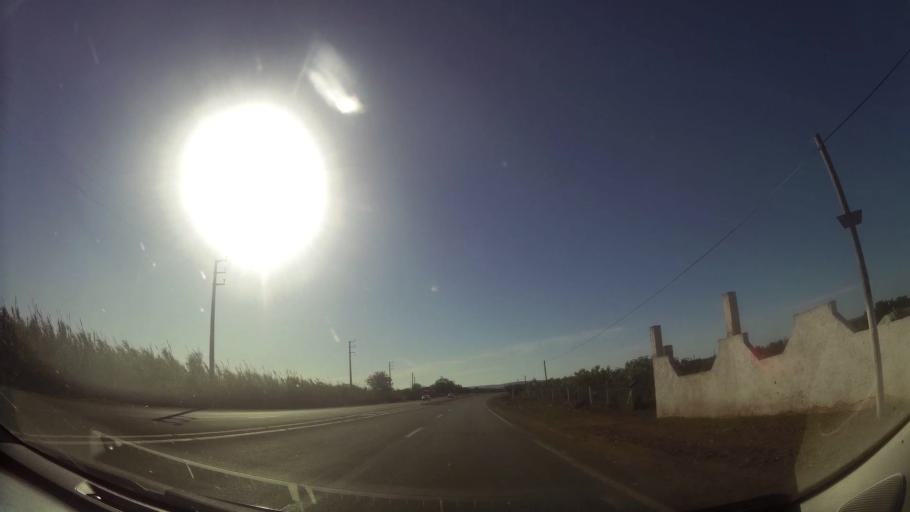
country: MA
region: Oriental
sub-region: Berkane-Taourirt
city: Ahfir
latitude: 35.0107
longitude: -2.1950
